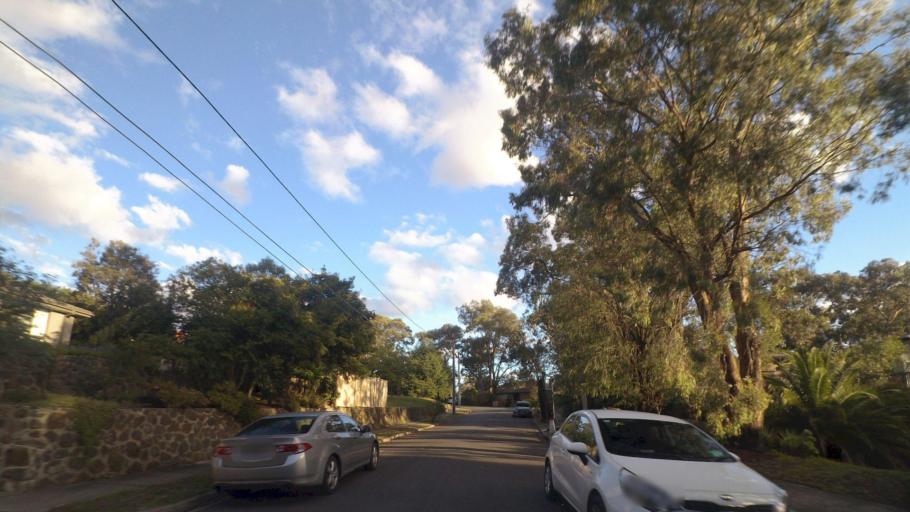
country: AU
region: Victoria
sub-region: Banyule
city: Lower Plenty
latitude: -37.7285
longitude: 145.1221
